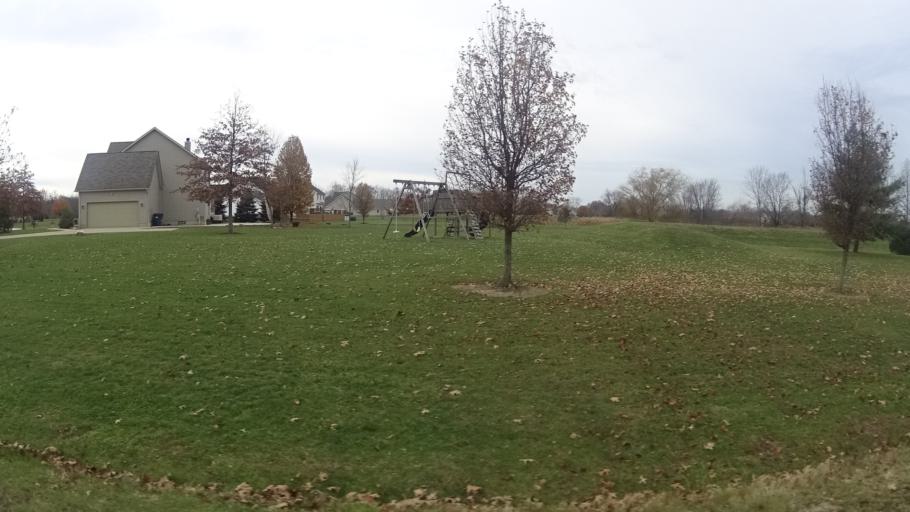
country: US
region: Ohio
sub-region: Lorain County
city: Eaton Estates
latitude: 41.2806
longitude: -81.9469
